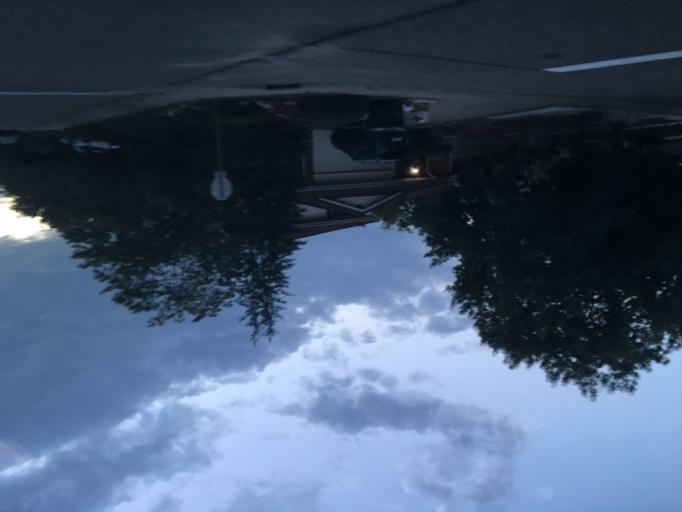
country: US
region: Colorado
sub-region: Adams County
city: Aurora
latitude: 39.6857
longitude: -104.8505
